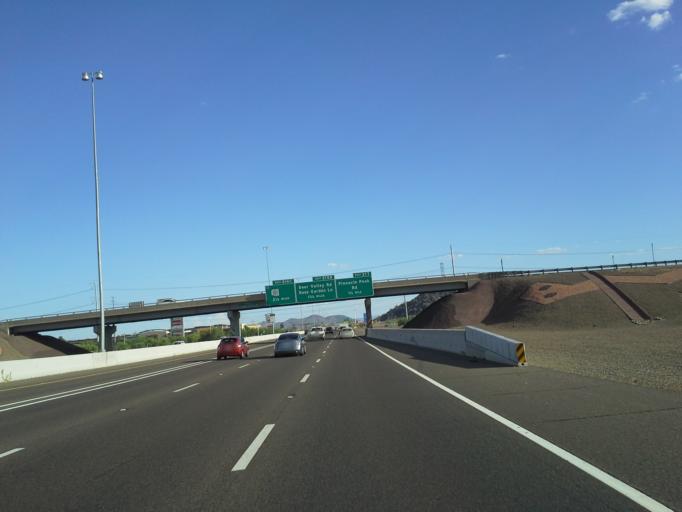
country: US
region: Arizona
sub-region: Maricopa County
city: Anthem
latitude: 33.7139
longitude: -112.1179
